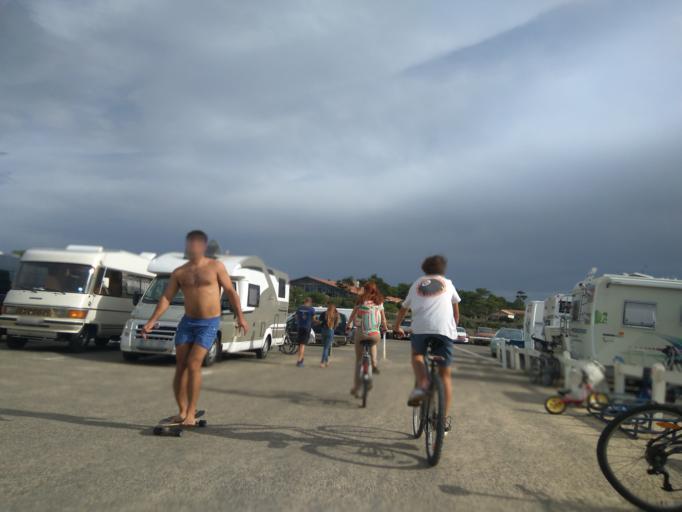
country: FR
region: Aquitaine
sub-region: Departement des Landes
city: Capbreton
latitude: 43.6362
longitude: -1.4474
